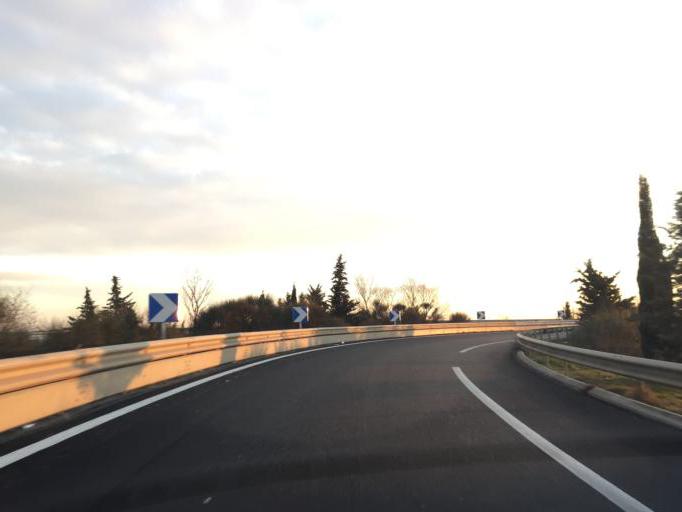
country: FR
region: Provence-Alpes-Cote d'Azur
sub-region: Departement du Vaucluse
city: Cavaillon
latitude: 43.8237
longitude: 5.0287
